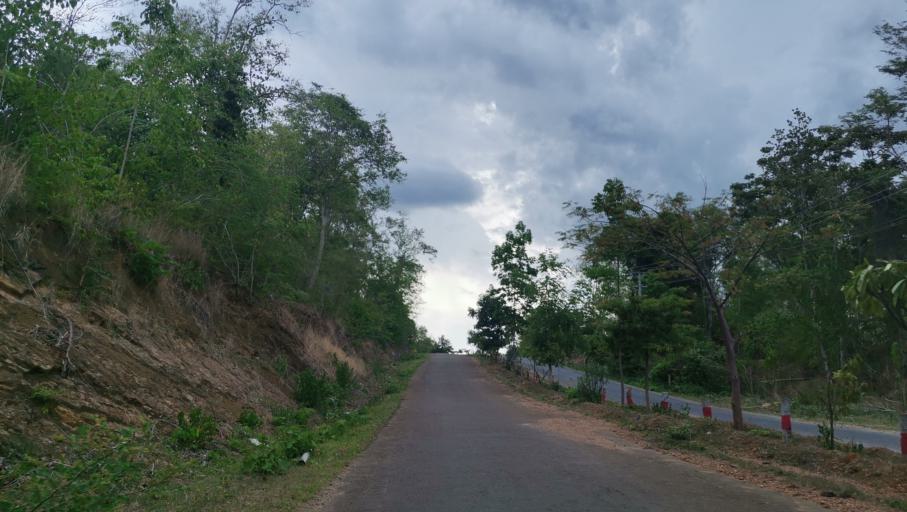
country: MM
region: Magway
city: Minbu
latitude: 20.0999
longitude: 94.5536
